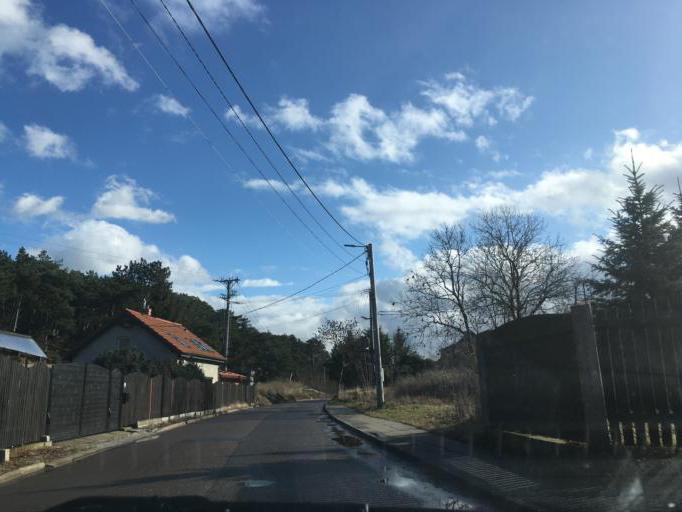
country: PL
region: Pomeranian Voivodeship
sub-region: Powiat gdanski
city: Cedry Wielkie
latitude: 54.3504
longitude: 18.7933
